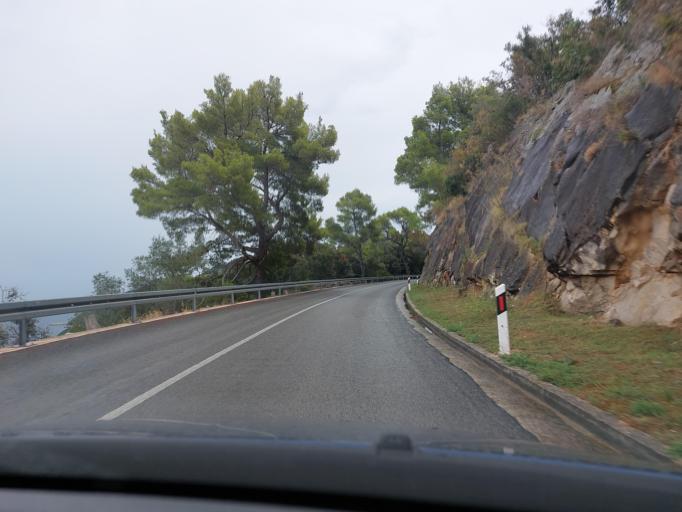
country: HR
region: Dubrovacko-Neretvanska
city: Smokvica
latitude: 42.7686
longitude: 16.8795
